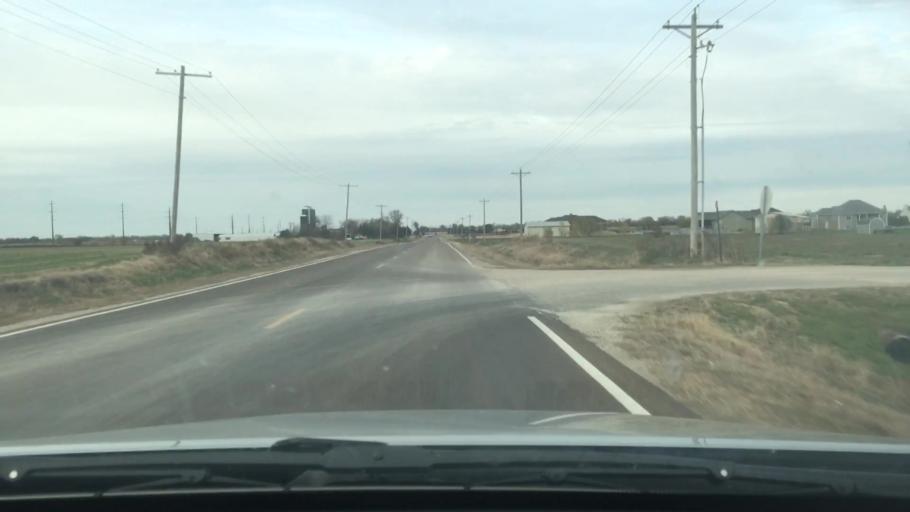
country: US
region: Kansas
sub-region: Sedgwick County
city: Colwich
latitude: 37.8110
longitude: -97.5186
